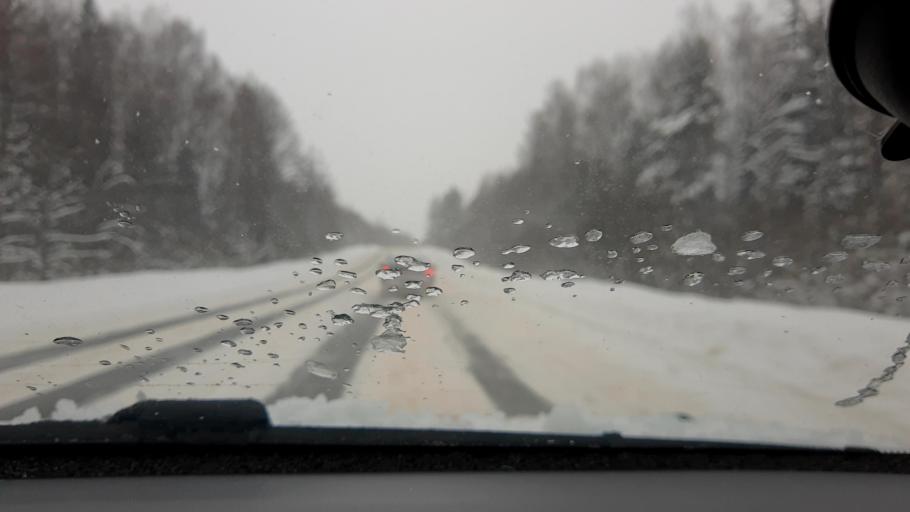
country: RU
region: Nizjnij Novgorod
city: Purekh
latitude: 56.6358
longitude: 43.1245
